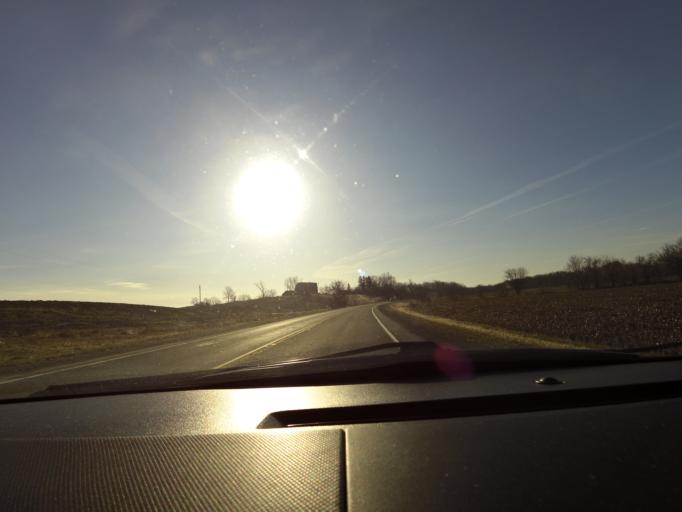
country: CA
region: Ontario
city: Ancaster
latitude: 43.0119
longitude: -79.8776
